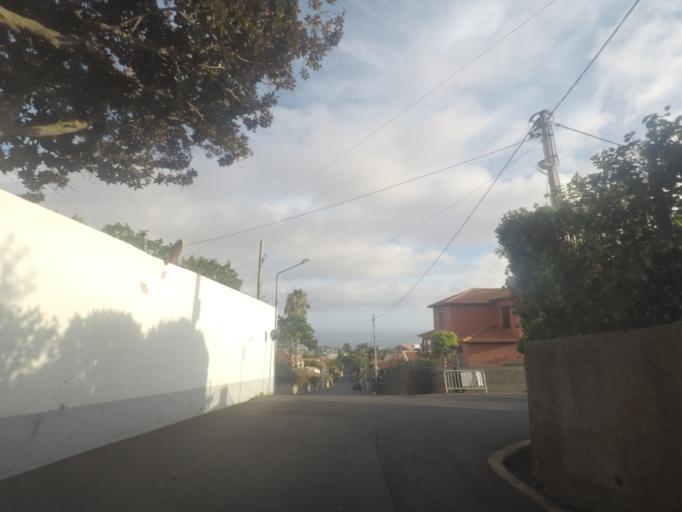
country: PT
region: Madeira
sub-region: Funchal
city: Nossa Senhora do Monte
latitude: 32.6681
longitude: -16.9405
